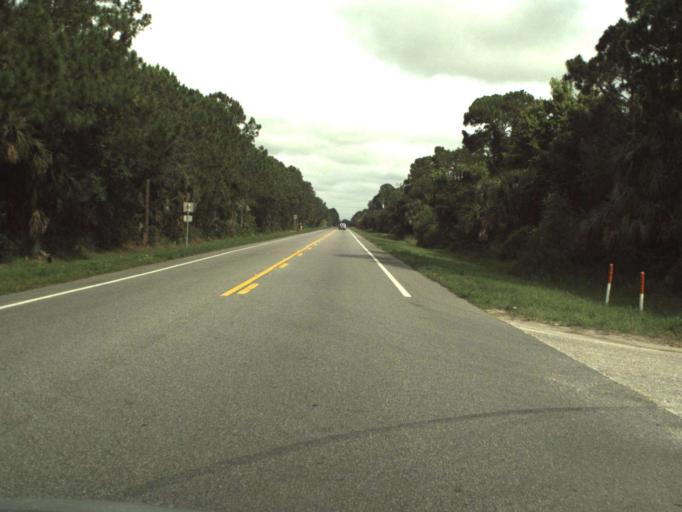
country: US
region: Florida
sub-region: Seminole County
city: Geneva
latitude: 28.7660
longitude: -81.1514
